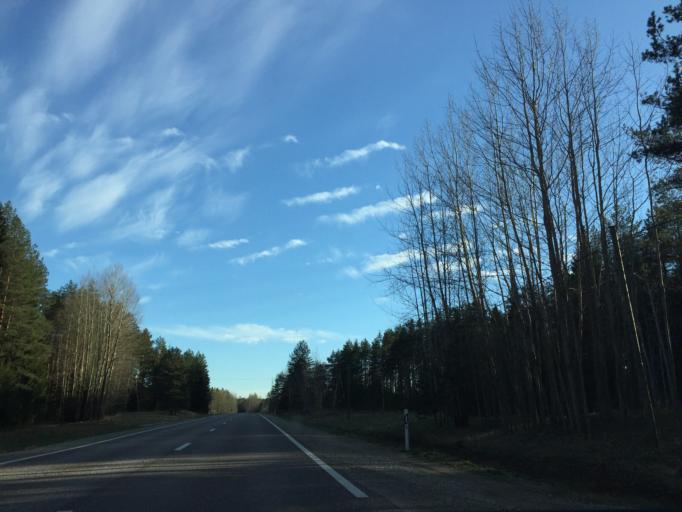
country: LV
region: Valkas Rajons
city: Valka
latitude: 57.7311
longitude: 25.9404
